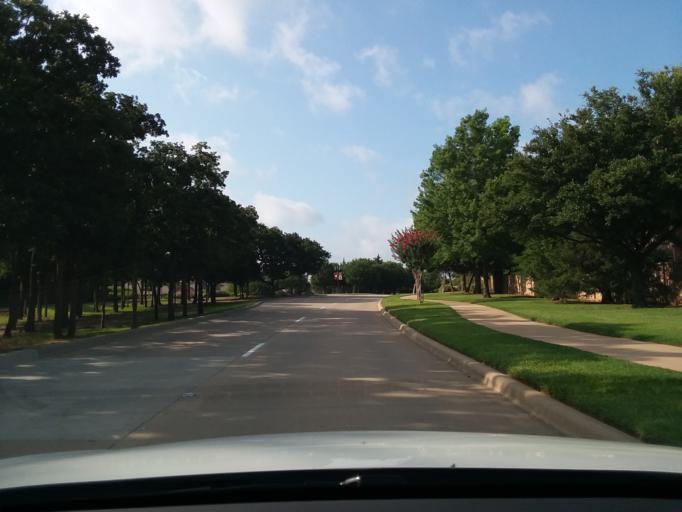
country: US
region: Texas
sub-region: Denton County
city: Copper Canyon
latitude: 33.0996
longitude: -97.1218
